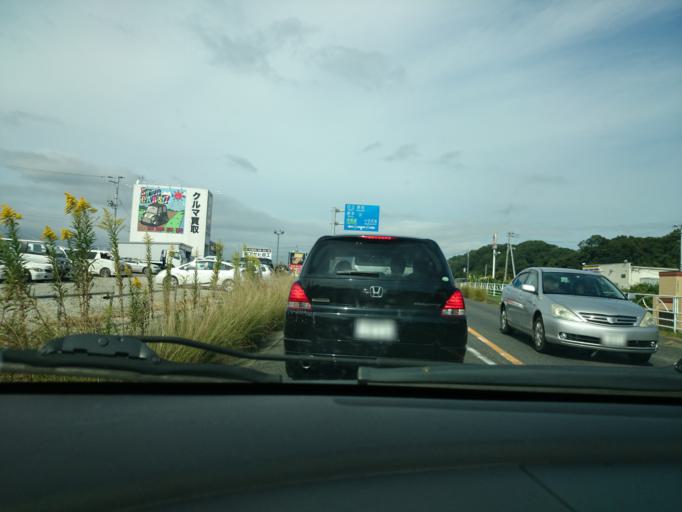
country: JP
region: Fukushima
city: Iwaki
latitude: 36.9717
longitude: 140.8912
